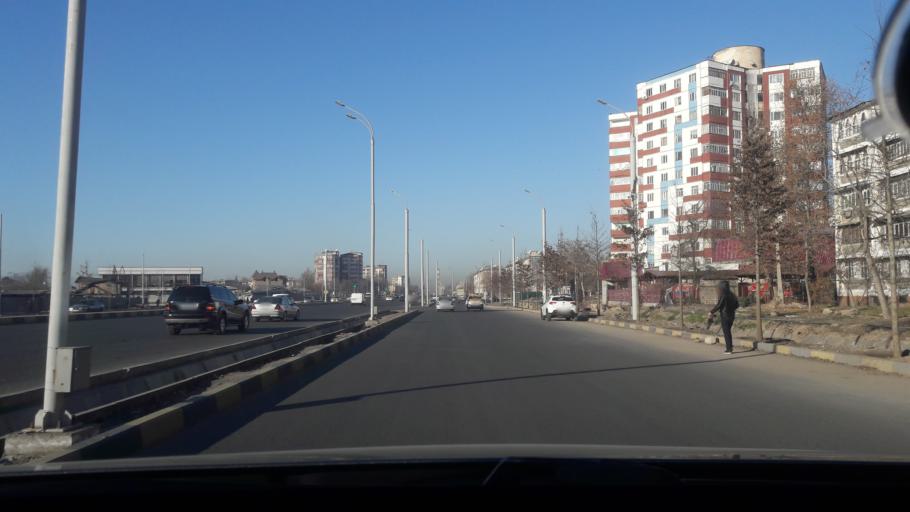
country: TJ
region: Dushanbe
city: Dushanbe
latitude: 38.5586
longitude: 68.7575
